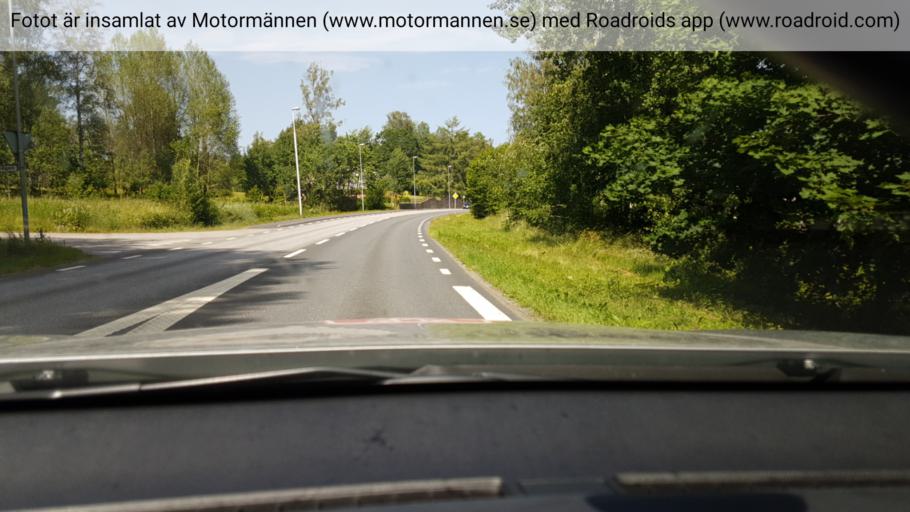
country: SE
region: Joenkoeping
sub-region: Nassjo Kommun
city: Bodafors
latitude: 57.5771
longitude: 14.8144
